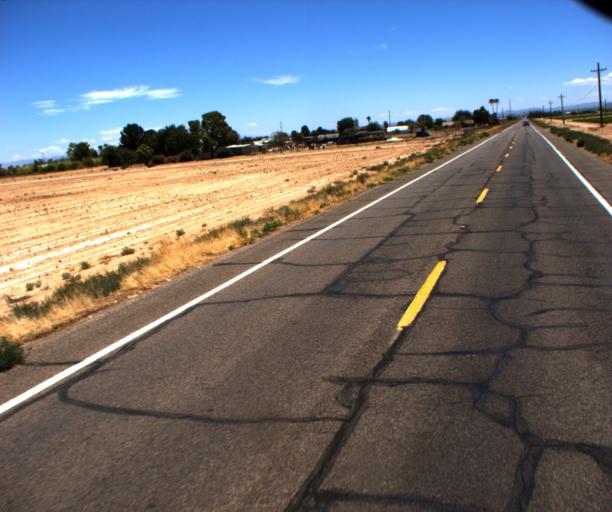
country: US
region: Arizona
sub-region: Pinal County
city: Coolidge
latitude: 32.8795
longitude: -111.5252
